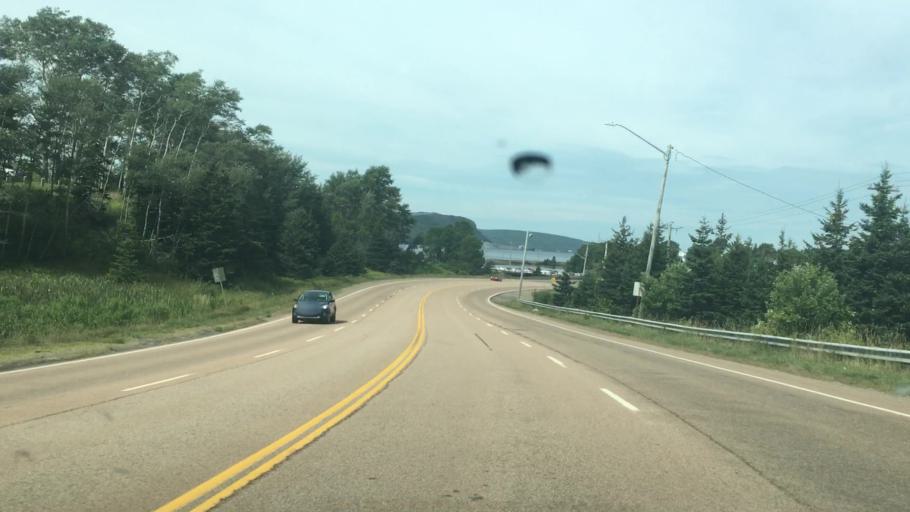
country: CA
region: Nova Scotia
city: Port Hawkesbury
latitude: 45.6209
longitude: -61.3615
